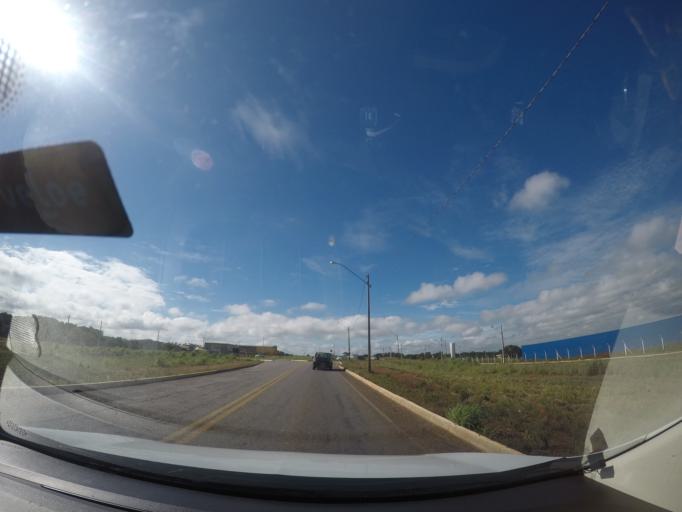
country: BR
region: Goias
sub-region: Senador Canedo
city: Senador Canedo
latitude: -16.6779
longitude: -49.1424
